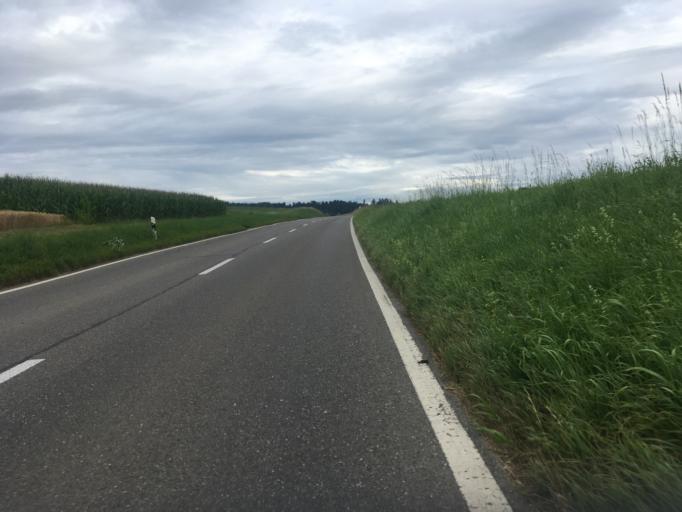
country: CH
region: Bern
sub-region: Seeland District
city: Erlach
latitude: 47.0323
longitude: 7.0941
